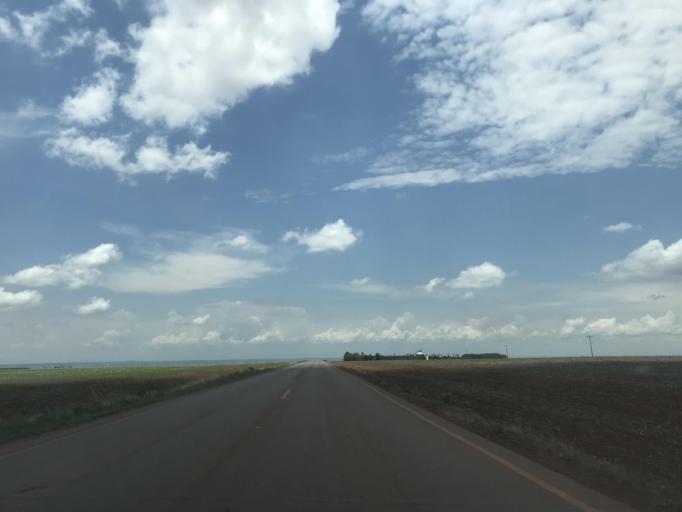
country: BR
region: Goias
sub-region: Vianopolis
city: Vianopolis
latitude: -16.5371
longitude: -48.2538
